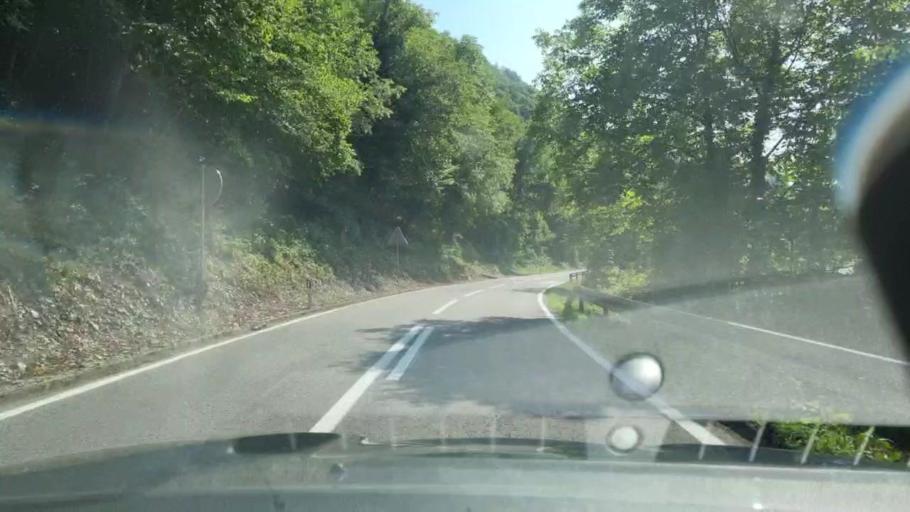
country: BA
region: Federation of Bosnia and Herzegovina
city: Bosanska Krupa
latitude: 44.8755
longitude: 16.1174
